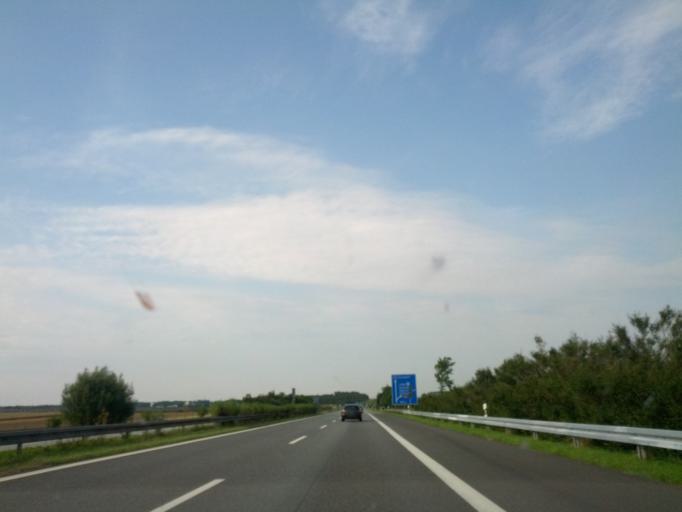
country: DE
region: Mecklenburg-Vorpommern
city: Laage
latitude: 53.8764
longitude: 12.2591
